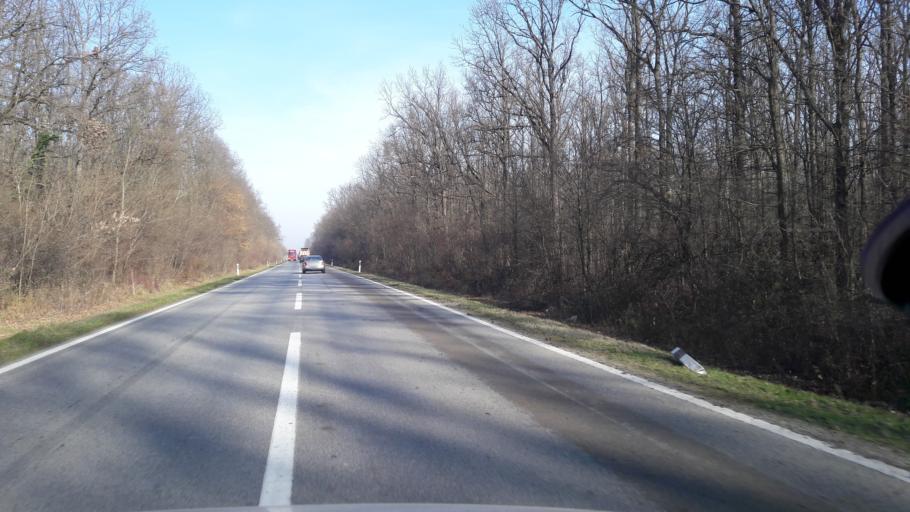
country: HR
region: Vukovarsko-Srijemska
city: Gradiste
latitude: 45.1270
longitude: 18.7150
